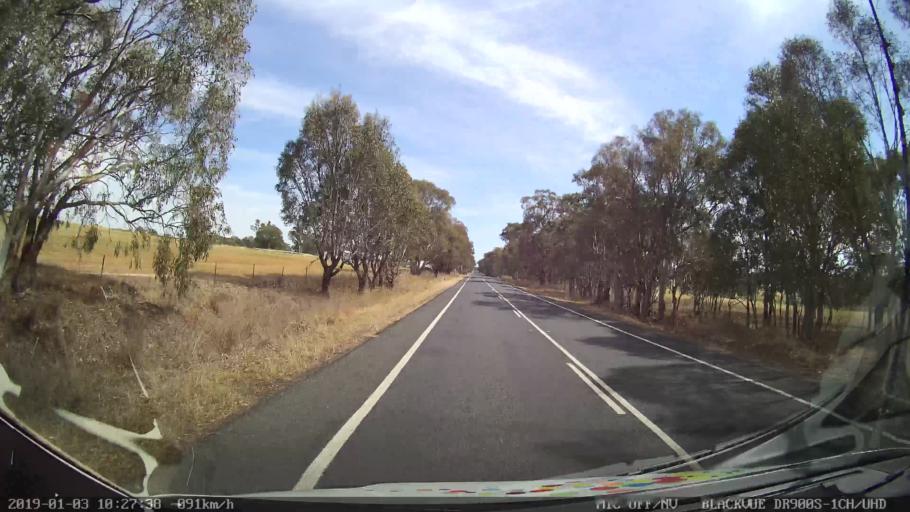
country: AU
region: New South Wales
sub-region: Young
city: Young
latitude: -34.3993
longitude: 148.2586
